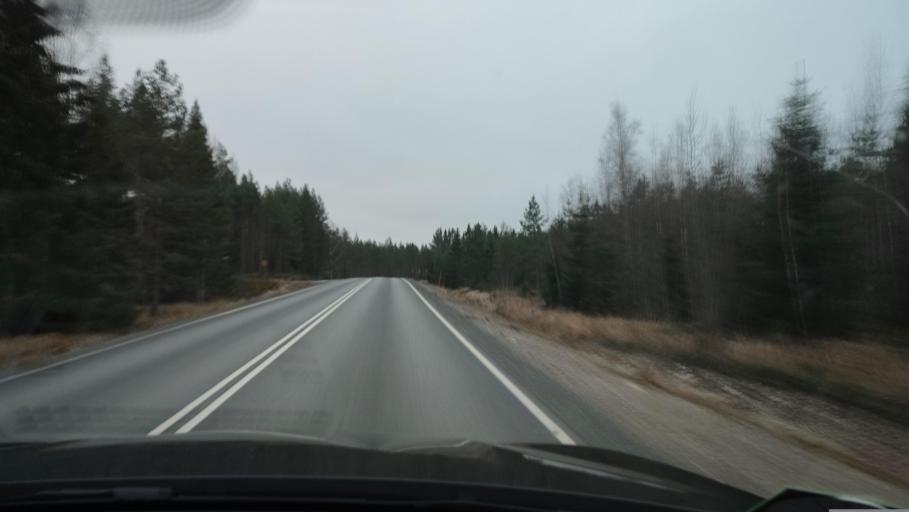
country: FI
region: Southern Ostrobothnia
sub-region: Suupohja
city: Karijoki
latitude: 62.2929
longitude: 21.6597
